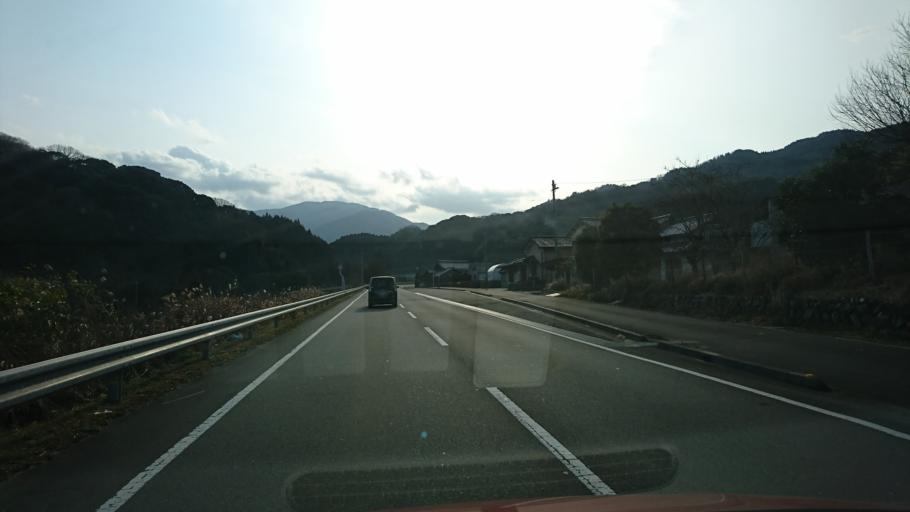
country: JP
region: Ehime
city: Hojo
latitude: 33.9896
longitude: 132.9116
